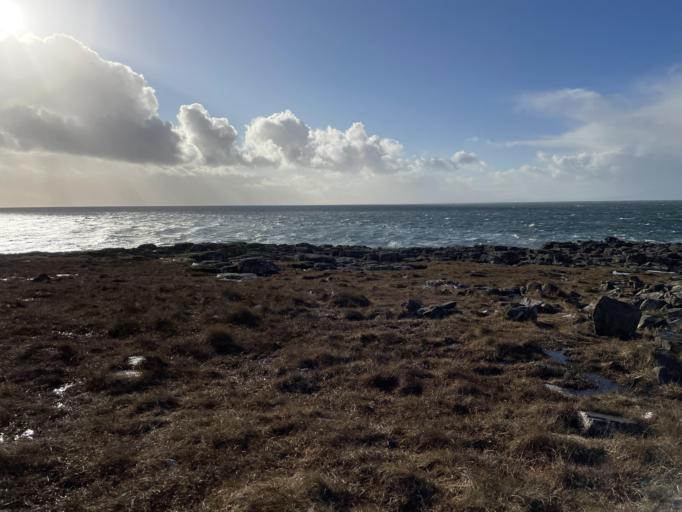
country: GB
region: Scotland
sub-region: Eilean Siar
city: Harris
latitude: 57.4213
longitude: -6.7870
